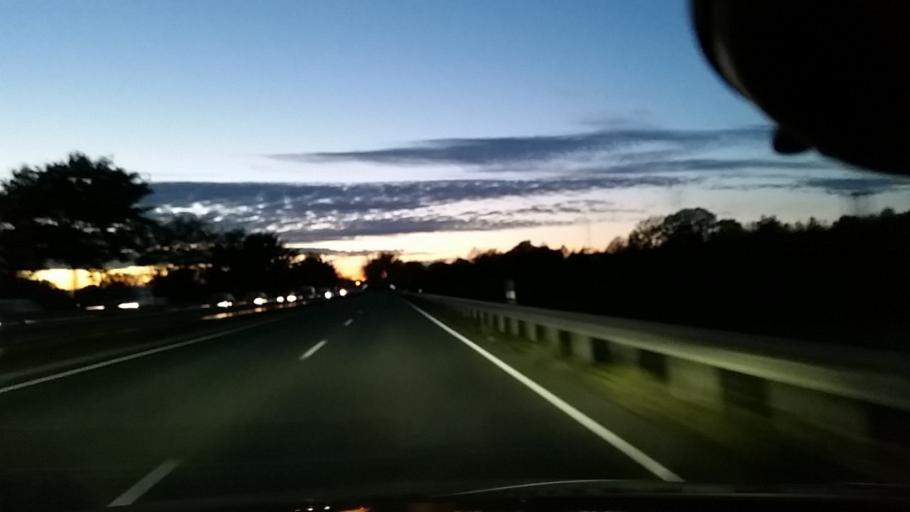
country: DE
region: Lower Saxony
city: Wolfsburg
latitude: 52.4400
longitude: 10.8212
